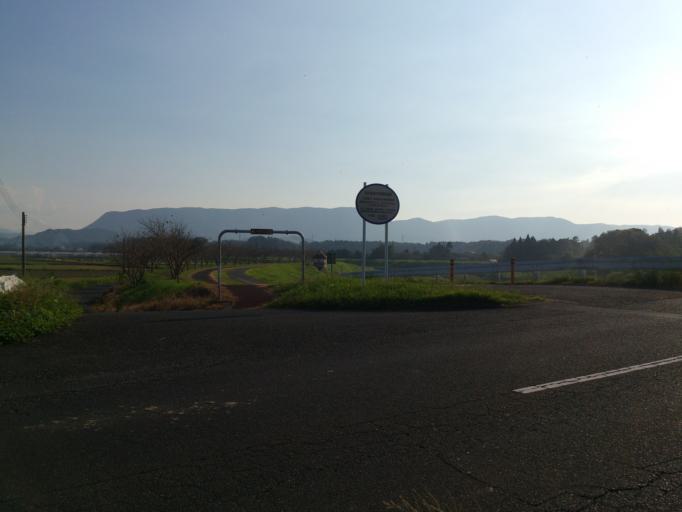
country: JP
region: Kagoshima
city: Kanoya
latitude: 31.3440
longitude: 130.9027
